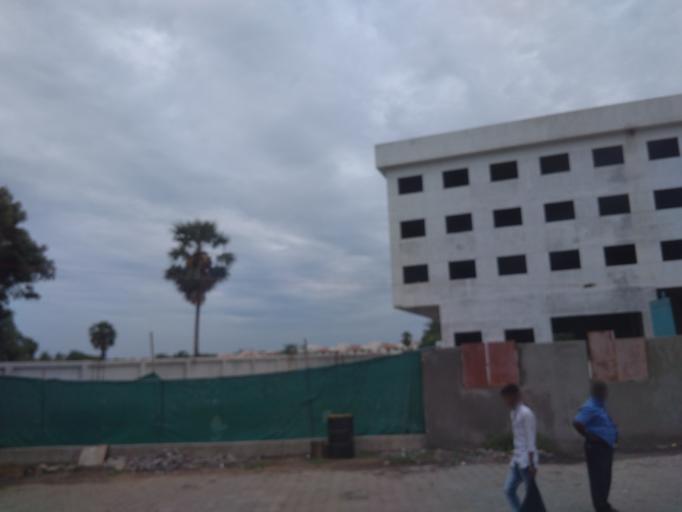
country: IN
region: Tamil Nadu
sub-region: Kancheepuram
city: Injambakkam
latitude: 12.8404
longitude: 80.2276
